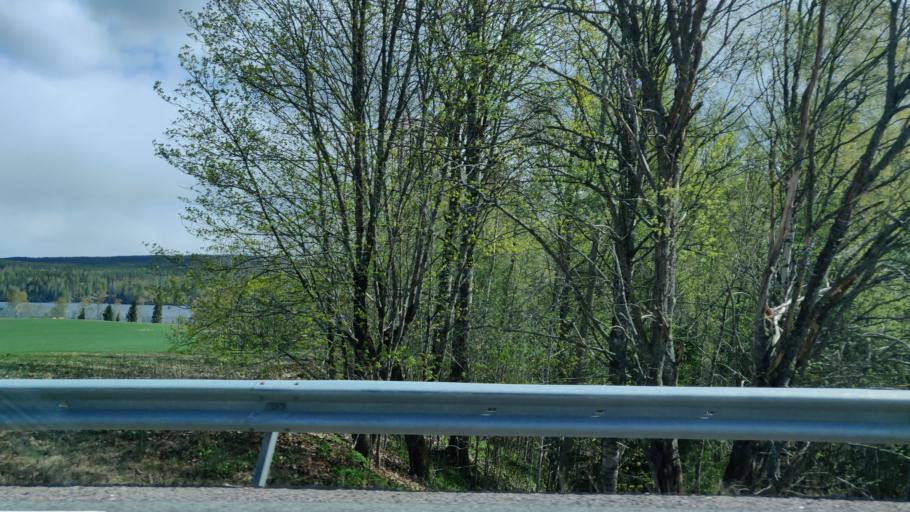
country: SE
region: Vaermland
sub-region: Munkfors Kommun
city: Munkfors
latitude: 59.8593
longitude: 13.7066
